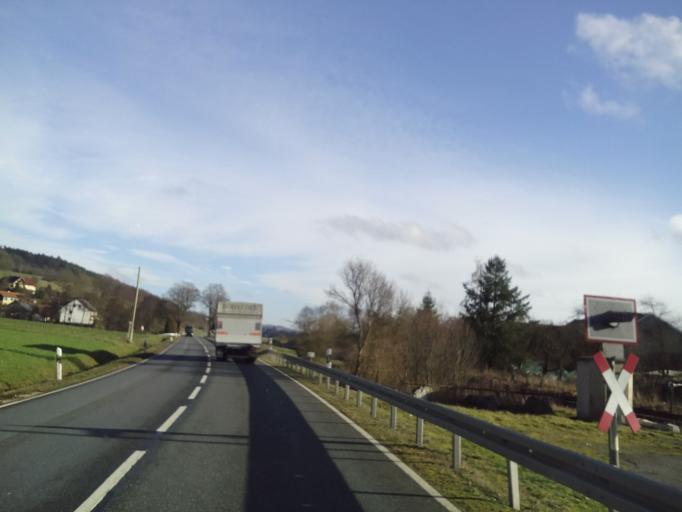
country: DE
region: Bavaria
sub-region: Upper Franconia
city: Altenkunstadt
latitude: 50.1257
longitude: 11.2936
